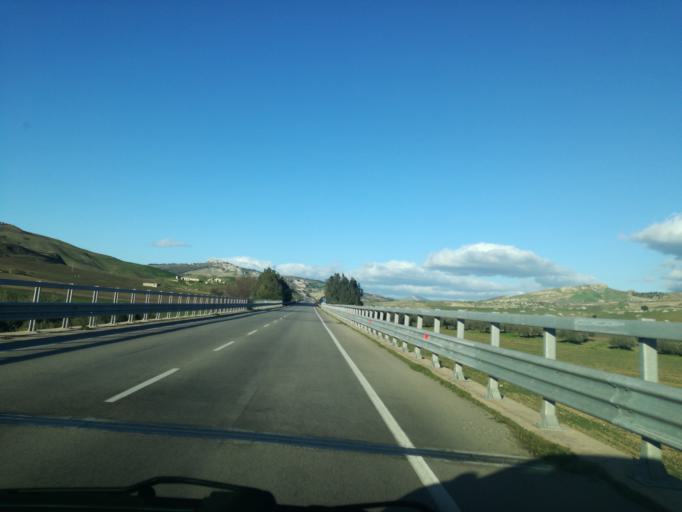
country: IT
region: Sicily
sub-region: Enna
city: Pietraperzia
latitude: 37.4069
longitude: 14.0647
